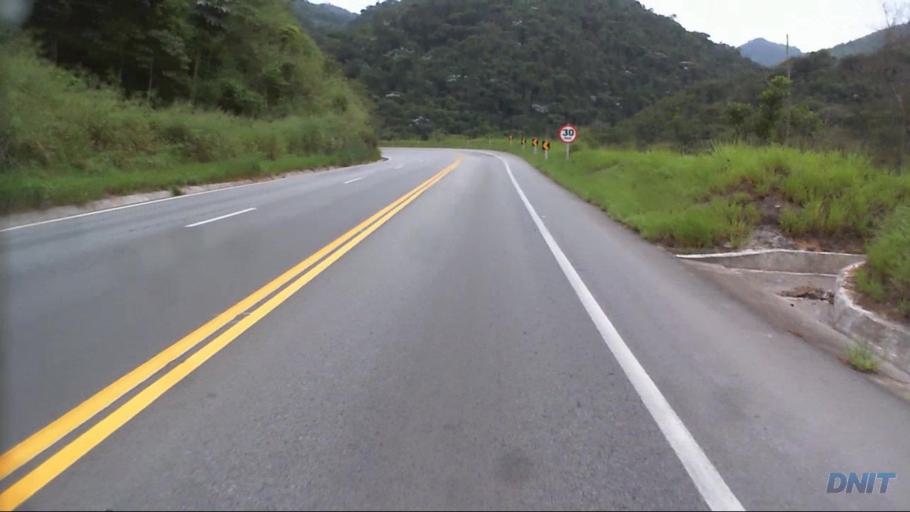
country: BR
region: Minas Gerais
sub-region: Nova Era
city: Nova Era
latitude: -19.6410
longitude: -42.9127
